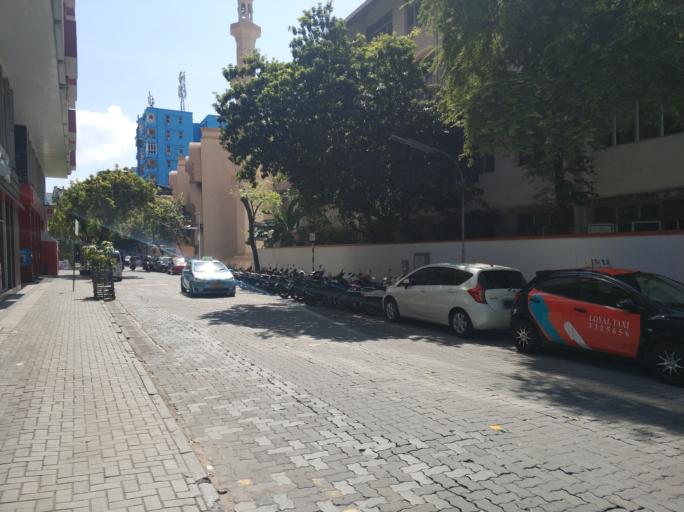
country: MV
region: Maale
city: Male
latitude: 4.1714
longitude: 73.5110
